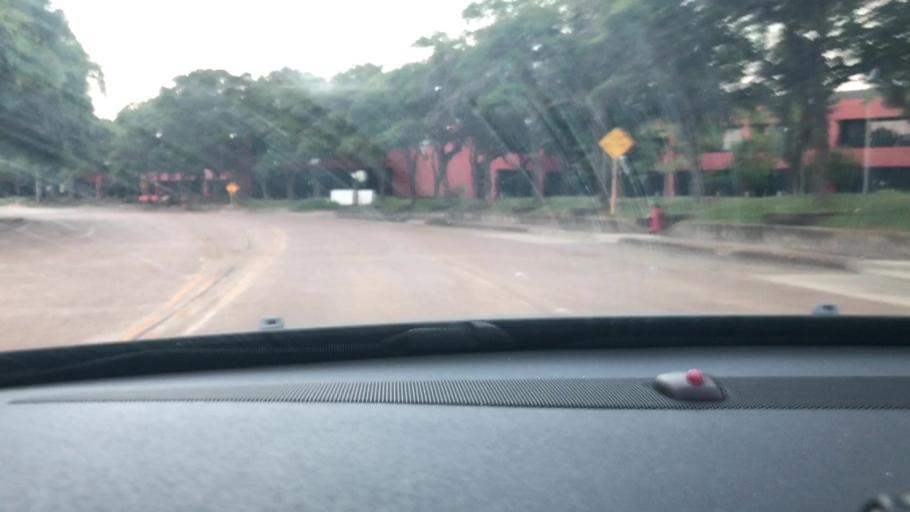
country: US
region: Texas
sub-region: Harris County
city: Webster
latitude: 29.5497
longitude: -95.1260
